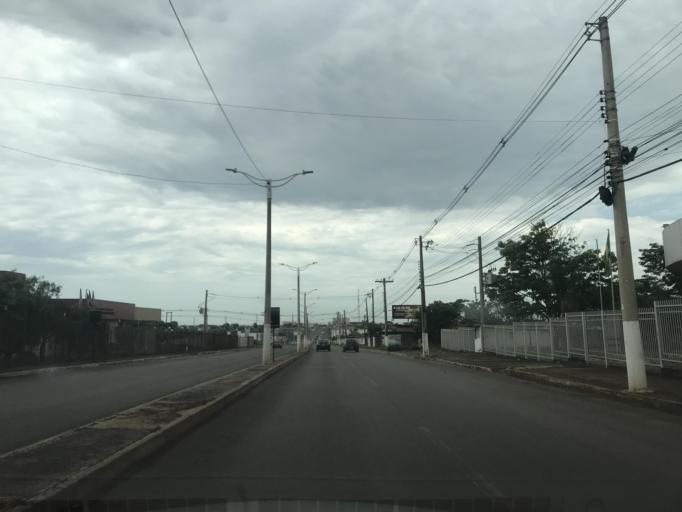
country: BR
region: Goias
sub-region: Luziania
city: Luziania
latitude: -16.2278
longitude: -47.9386
